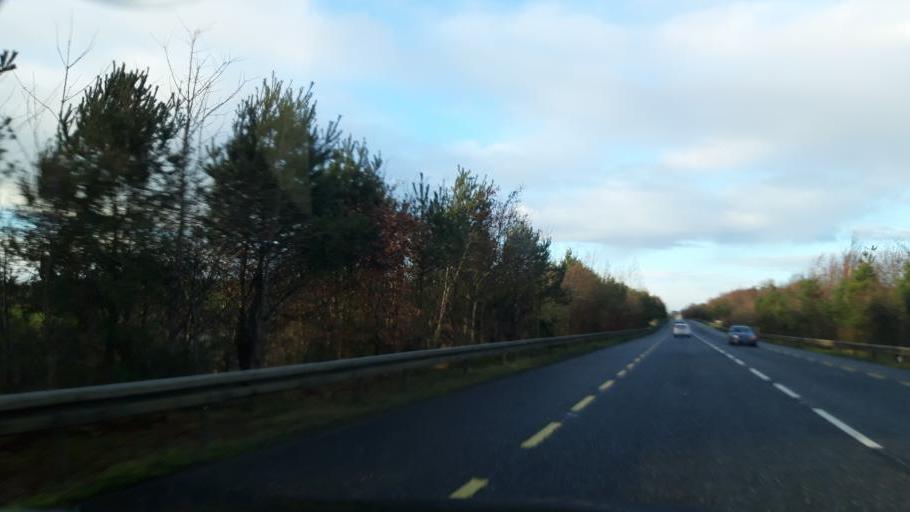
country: IE
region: Ulster
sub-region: County Monaghan
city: Carrickmacross
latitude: 53.9493
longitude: -6.6711
